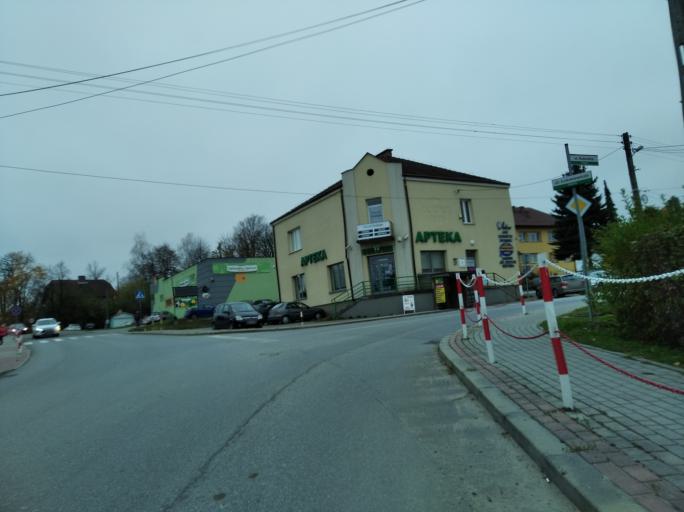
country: PL
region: Subcarpathian Voivodeship
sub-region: Powiat krosnienski
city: Chorkowka
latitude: 49.6678
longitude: 21.6906
